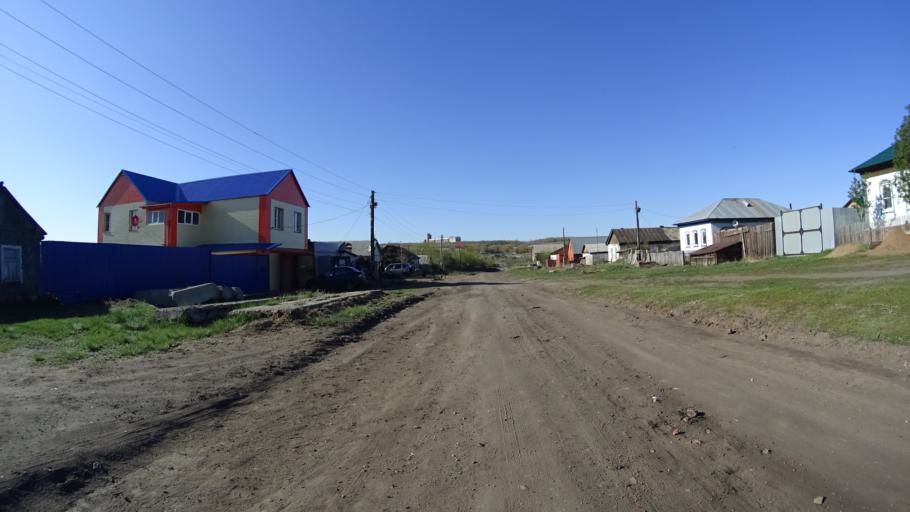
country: RU
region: Chelyabinsk
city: Troitsk
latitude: 54.0923
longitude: 61.5999
